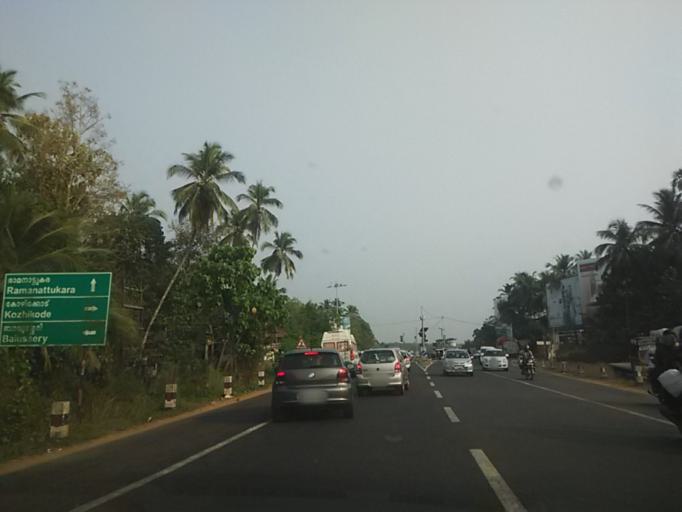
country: IN
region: Kerala
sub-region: Kozhikode
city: Kozhikode
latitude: 11.3025
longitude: 75.7914
